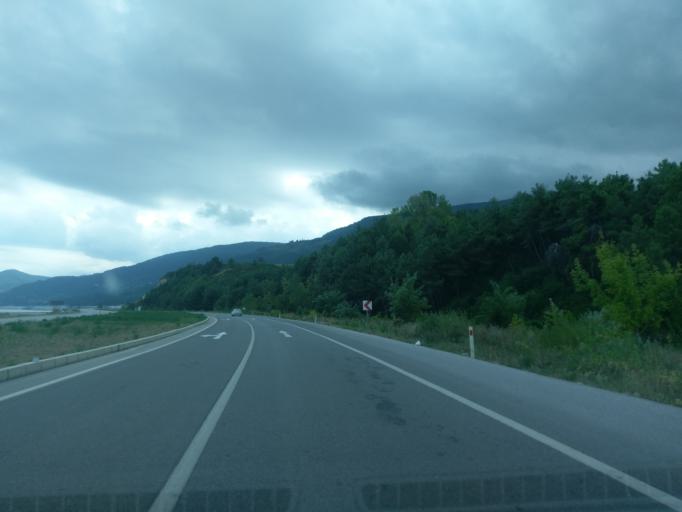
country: TR
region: Sinop
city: Gerze
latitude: 41.7746
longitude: 35.2032
